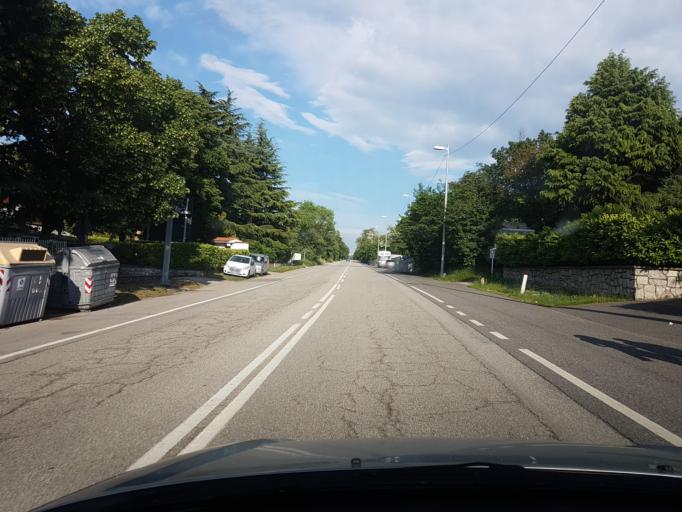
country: IT
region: Friuli Venezia Giulia
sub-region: Provincia di Trieste
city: Villa Opicina
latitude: 45.6824
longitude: 13.7865
